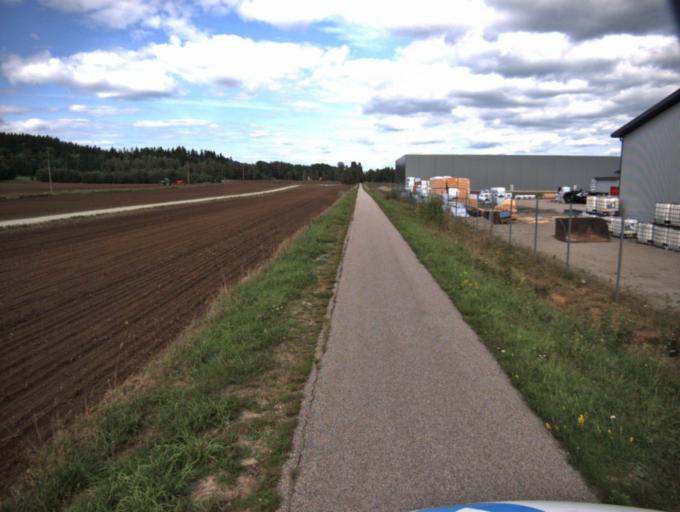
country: SE
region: Vaestra Goetaland
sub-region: Ulricehamns Kommun
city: Ulricehamn
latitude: 57.8383
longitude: 13.4205
